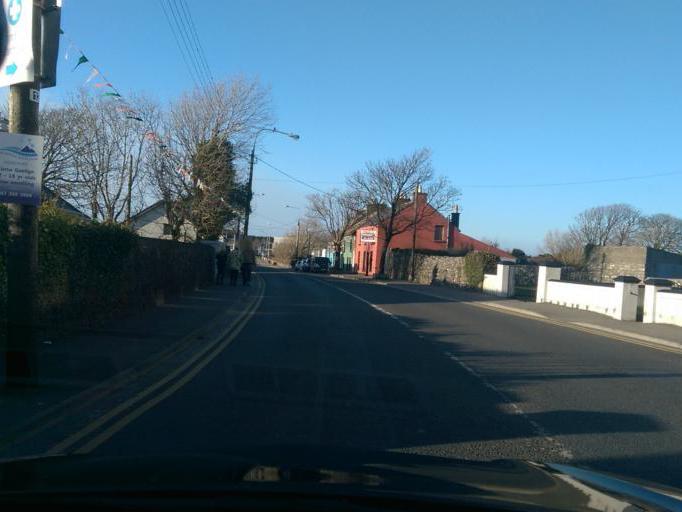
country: IE
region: Connaught
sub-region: County Galway
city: Oranmore
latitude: 53.2700
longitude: -8.9286
